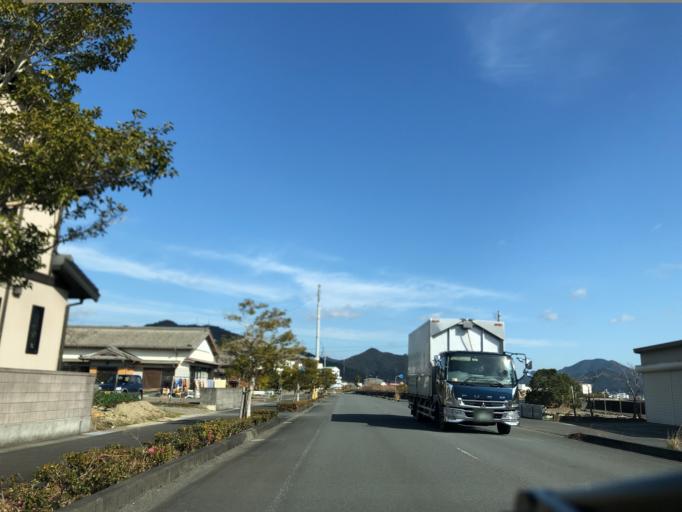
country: JP
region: Kochi
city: Sukumo
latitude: 32.9226
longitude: 132.7018
